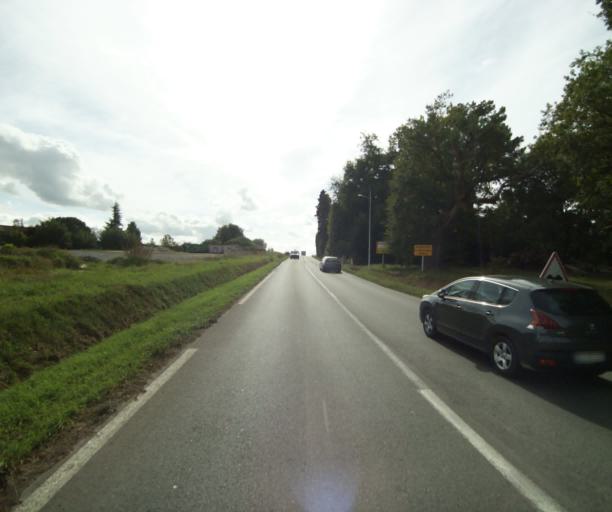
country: FR
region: Midi-Pyrenees
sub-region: Departement du Gers
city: Eauze
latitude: 43.8517
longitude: 0.0962
